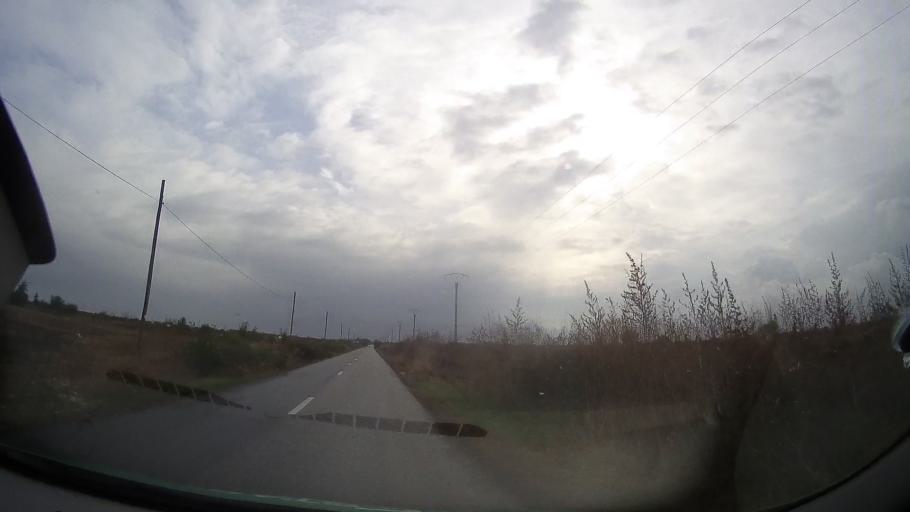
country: RO
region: Ialomita
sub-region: Comuna Fierbinti-Targ
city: Fierbintii de Jos
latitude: 44.7099
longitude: 26.3914
